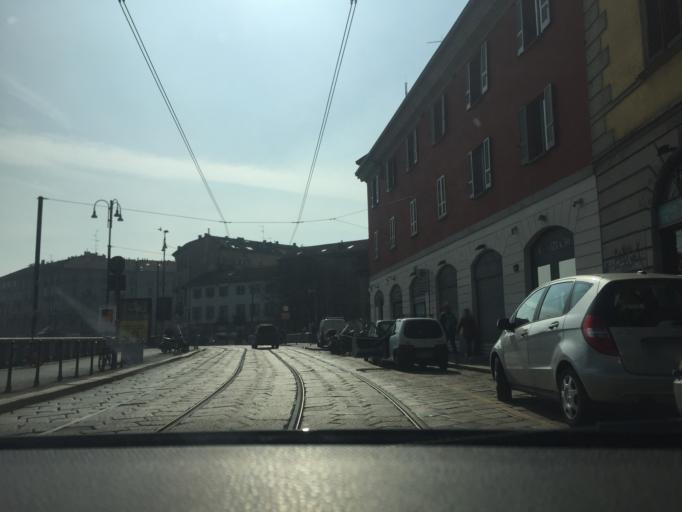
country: IT
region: Lombardy
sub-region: Citta metropolitana di Milano
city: Milano
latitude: 45.4527
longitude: 9.1761
